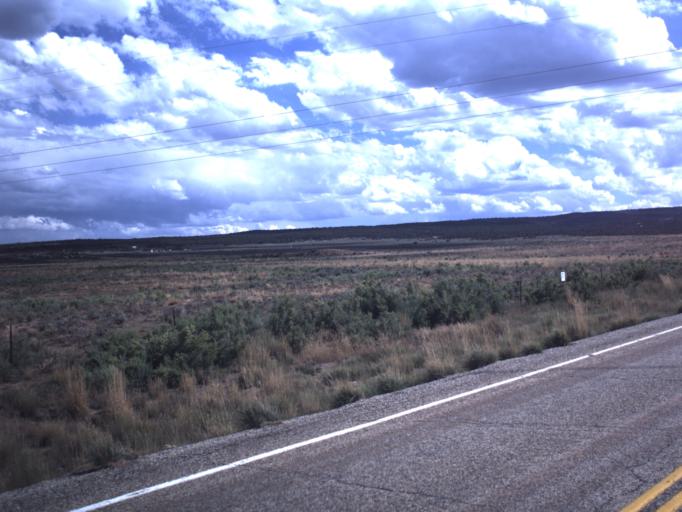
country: US
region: Utah
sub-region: Duchesne County
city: Duchesne
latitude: 40.2197
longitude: -110.7250
